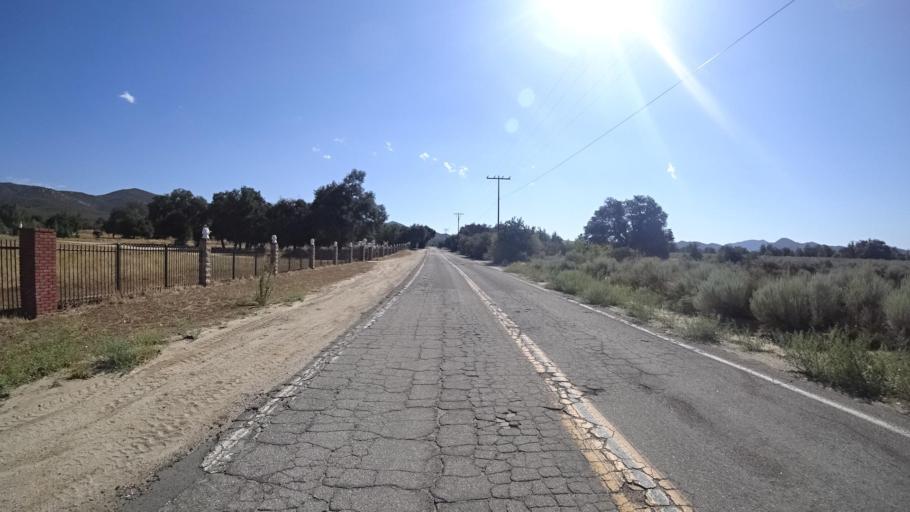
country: US
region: California
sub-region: Riverside County
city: Anza
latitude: 33.3846
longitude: -116.6583
